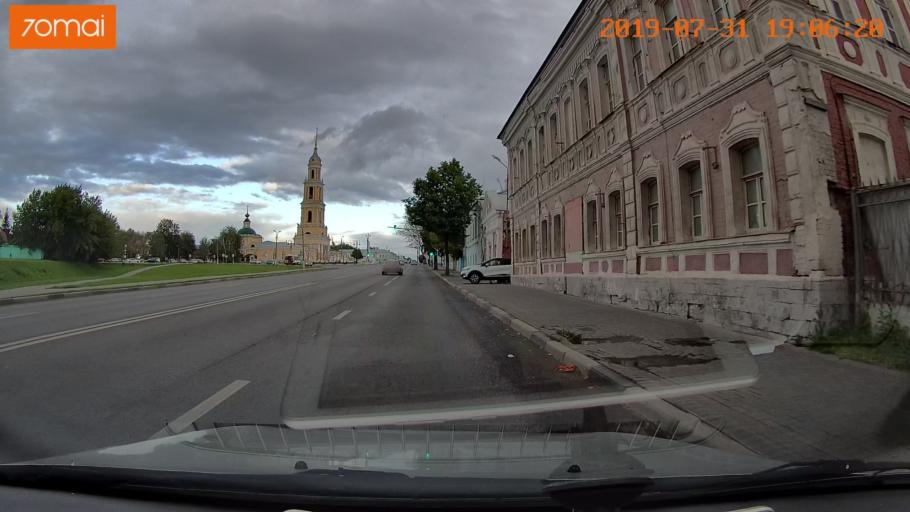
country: RU
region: Moskovskaya
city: Kolomna
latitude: 55.1029
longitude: 38.7520
